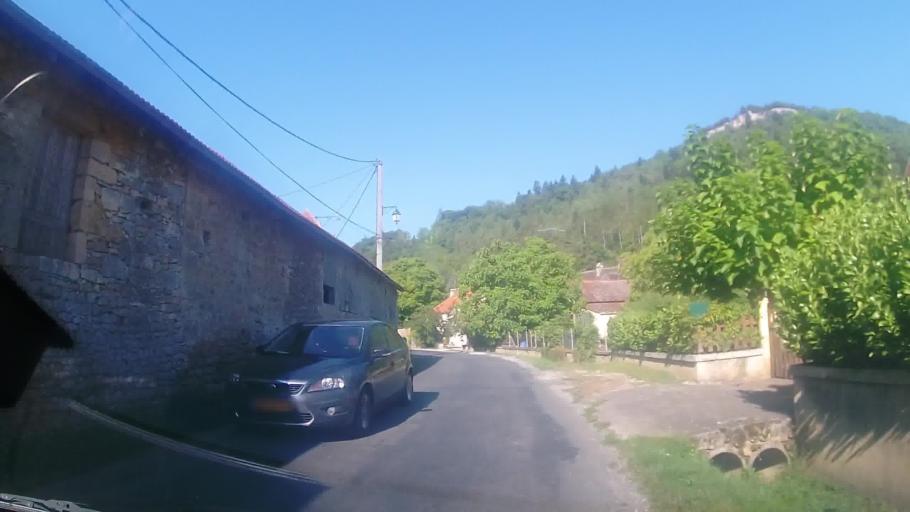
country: FR
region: Aquitaine
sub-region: Departement de la Dordogne
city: Cenac-et-Saint-Julien
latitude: 44.7960
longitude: 1.1611
